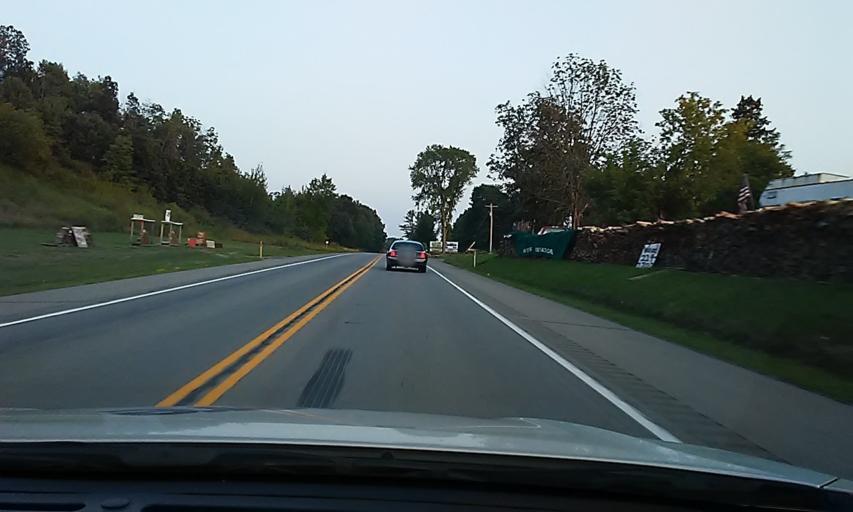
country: US
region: Pennsylvania
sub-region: Clarion County
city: Marianne
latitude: 41.2152
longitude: -79.4339
